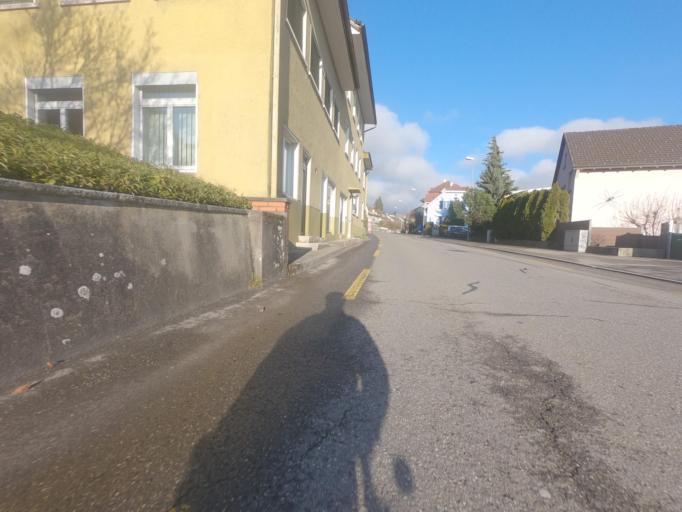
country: CH
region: Solothurn
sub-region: Bezirk Lebern
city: Grenchen
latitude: 47.1944
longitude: 7.4014
